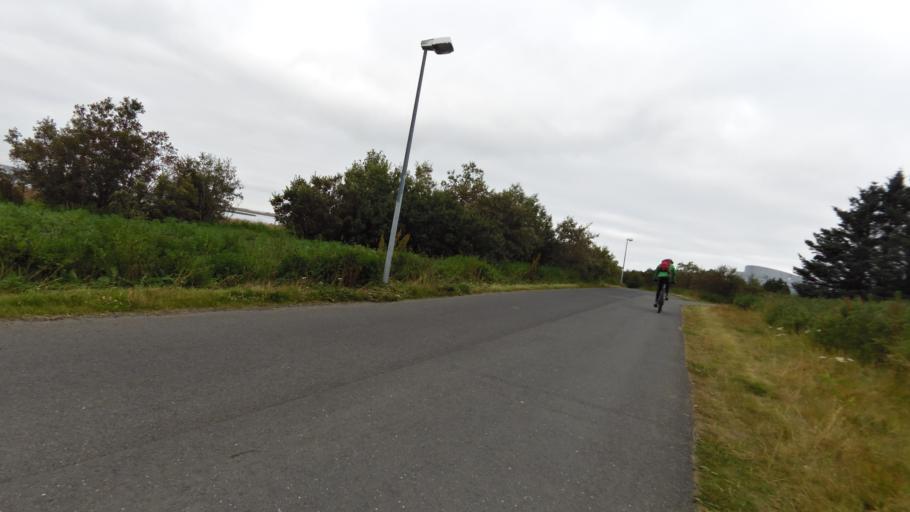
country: IS
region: Capital Region
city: Kopavogur
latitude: 64.1222
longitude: -21.9221
